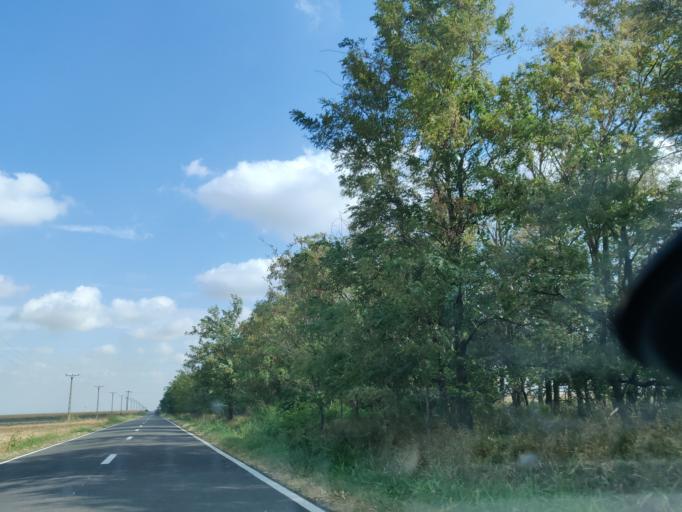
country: RO
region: Vrancea
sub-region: Comuna Maicanesti
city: Ramniceni
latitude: 45.4562
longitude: 27.4066
